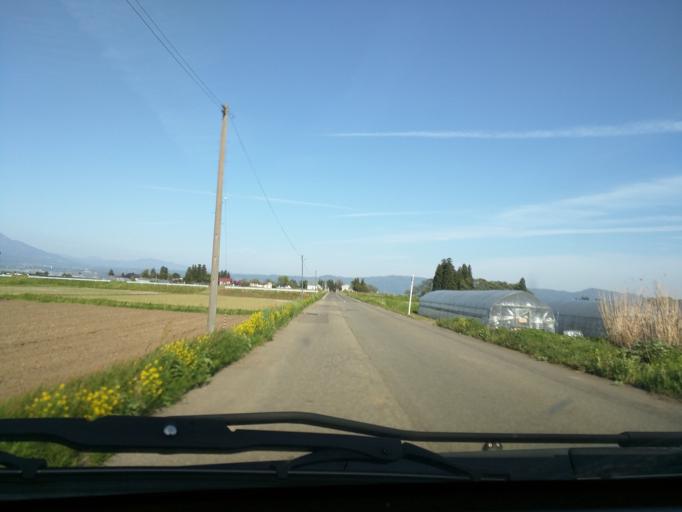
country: JP
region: Fukushima
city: Kitakata
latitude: 37.5214
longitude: 139.8094
